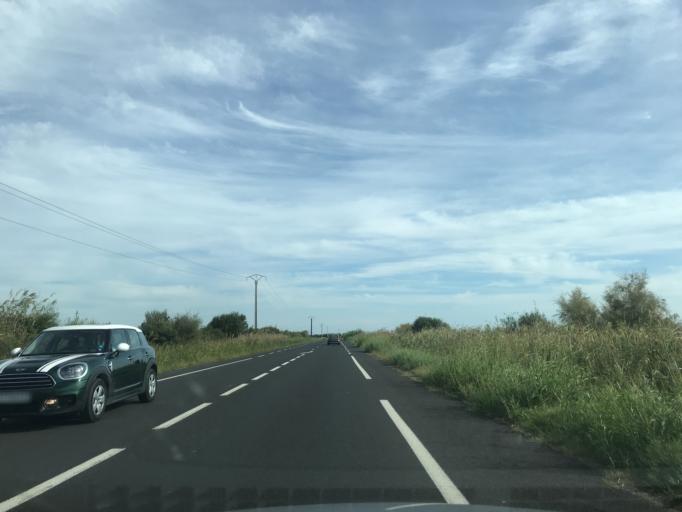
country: FR
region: Languedoc-Roussillon
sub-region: Departement du Gard
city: Aigues-Mortes
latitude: 43.5696
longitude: 4.3095
